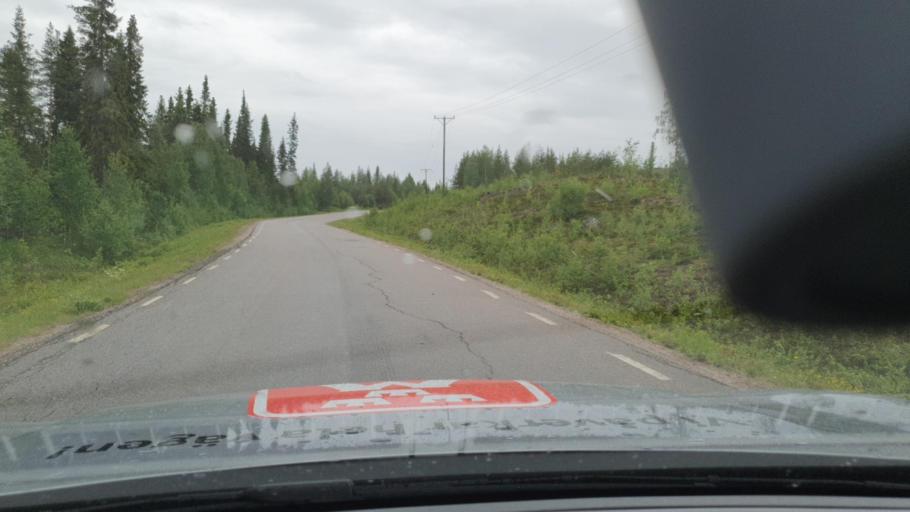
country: SE
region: Norrbotten
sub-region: Pajala Kommun
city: Pajala
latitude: 66.7743
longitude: 23.1436
